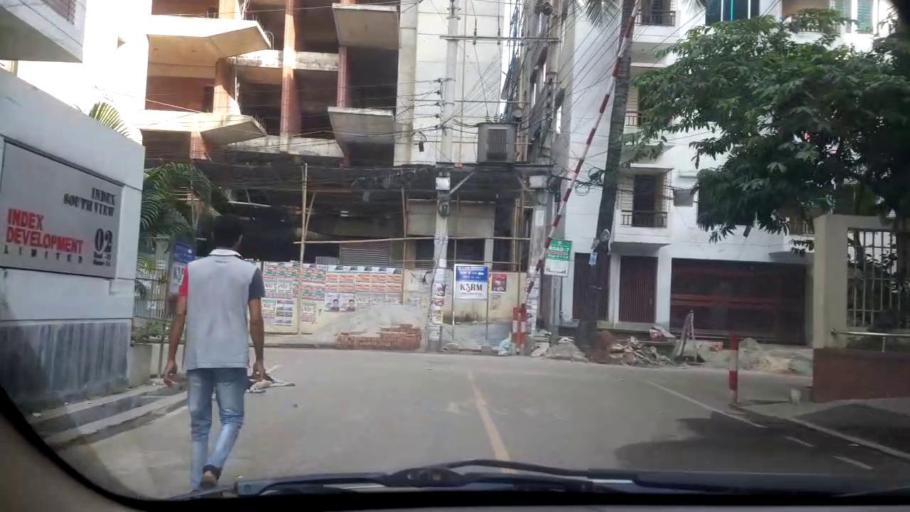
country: BD
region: Dhaka
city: Tungi
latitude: 23.8659
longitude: 90.3897
